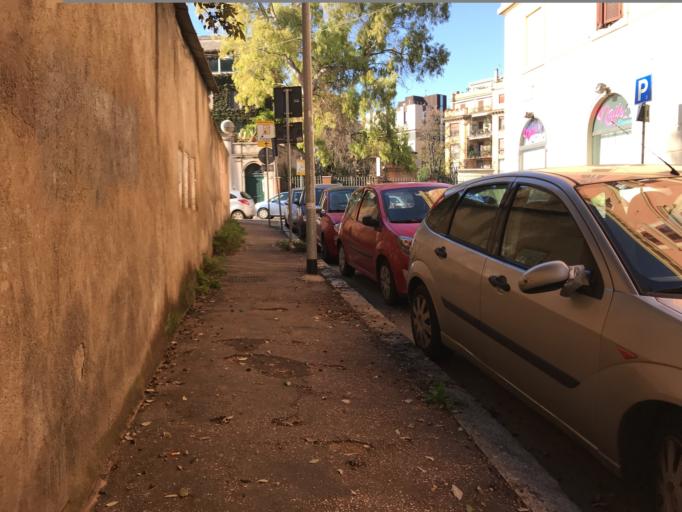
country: IT
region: Latium
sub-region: Citta metropolitana di Roma Capitale
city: Rome
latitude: 41.9151
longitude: 12.4976
